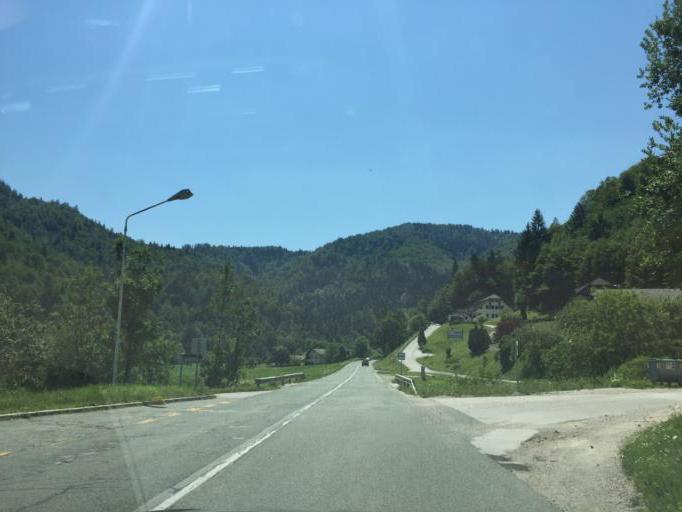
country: SI
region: Skofja Loka
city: Skofja Loka
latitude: 46.1432
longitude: 14.2738
